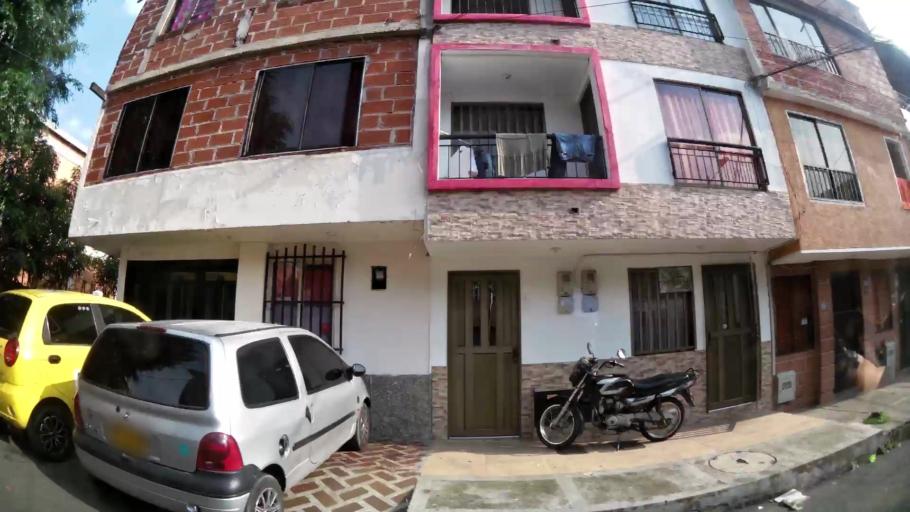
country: CO
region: Antioquia
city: Sabaneta
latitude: 6.1632
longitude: -75.6270
